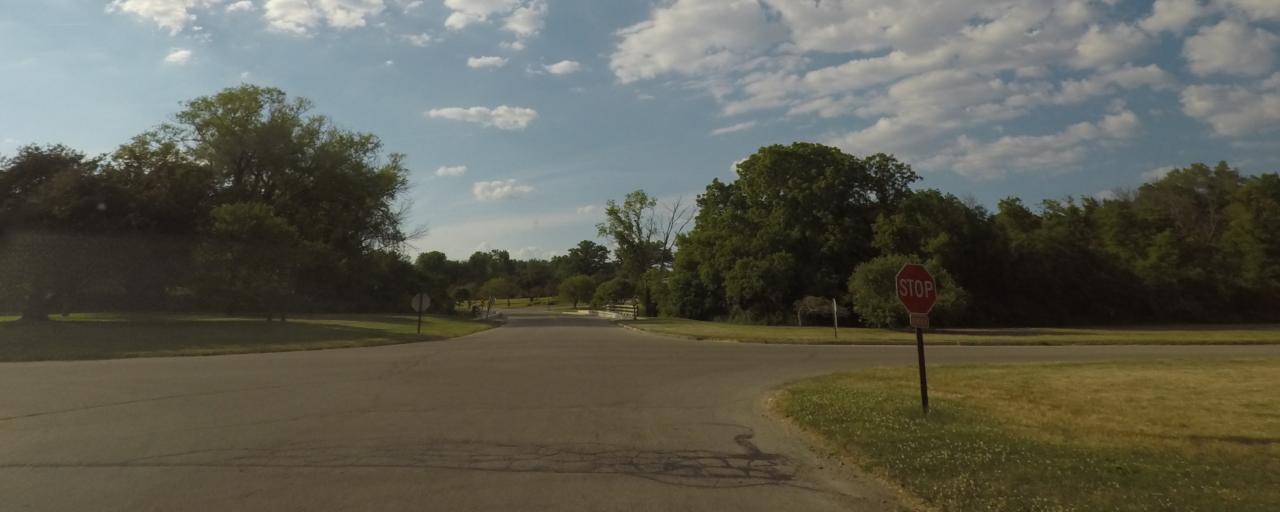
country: US
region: Wisconsin
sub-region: Milwaukee County
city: Hales Corners
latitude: 42.9302
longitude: -88.0295
